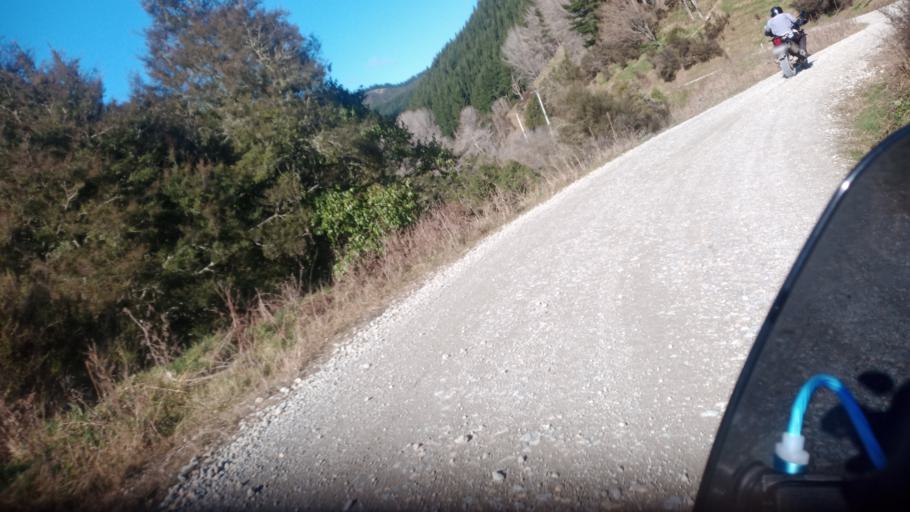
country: NZ
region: Hawke's Bay
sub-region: Wairoa District
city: Wairoa
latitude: -38.6587
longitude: 177.4995
